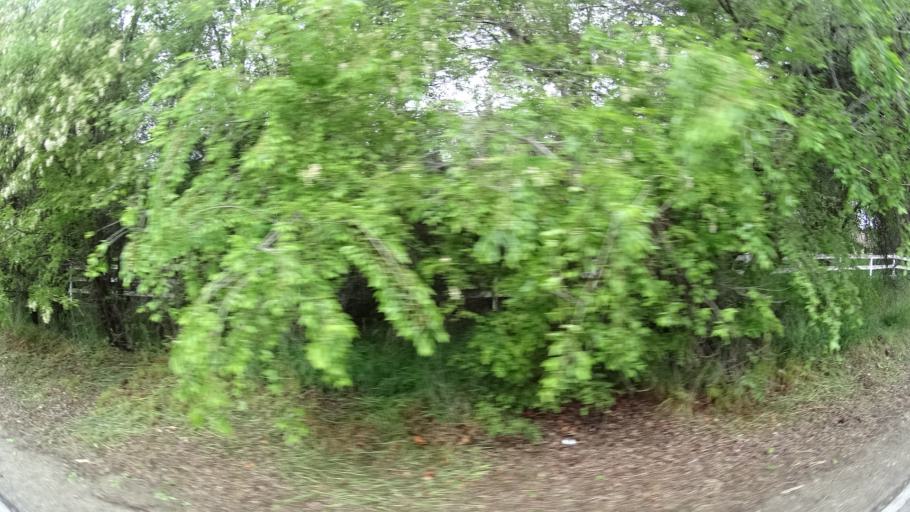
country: US
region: Idaho
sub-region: Ada County
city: Eagle
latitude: 43.7190
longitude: -116.3542
